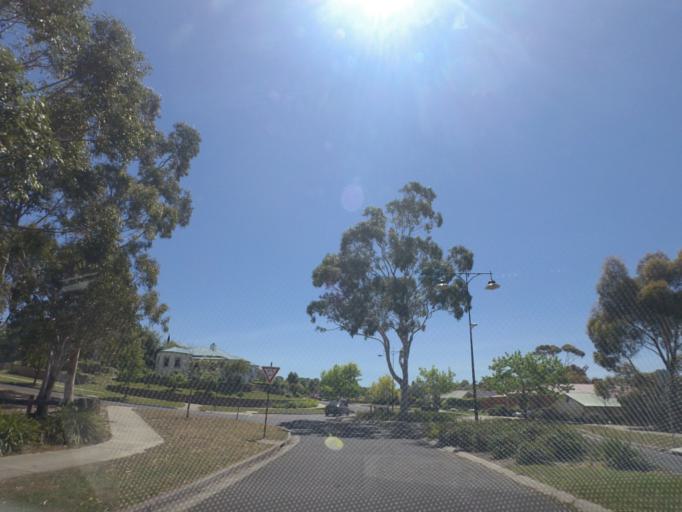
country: AU
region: Victoria
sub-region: Hume
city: Sunbury
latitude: -37.5581
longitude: 144.7114
